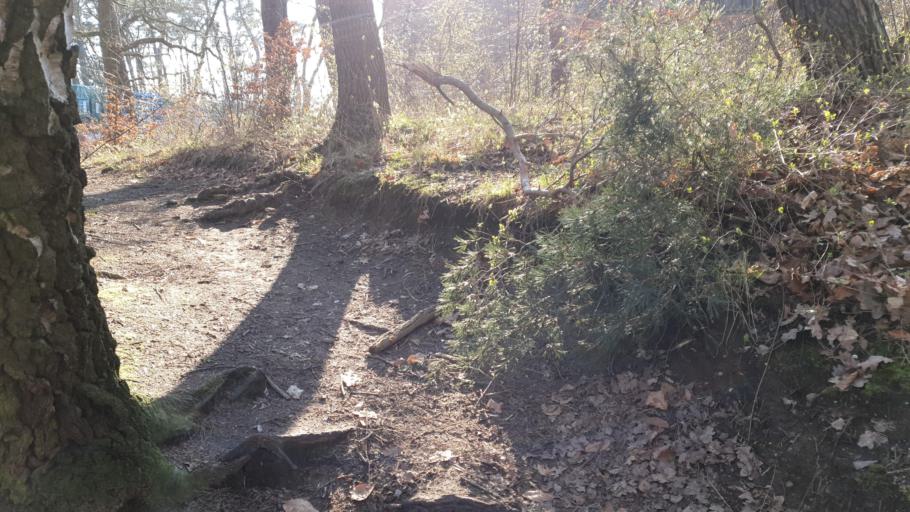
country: DE
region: Mecklenburg-Vorpommern
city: Wittenforden
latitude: 53.6375
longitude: 11.3433
